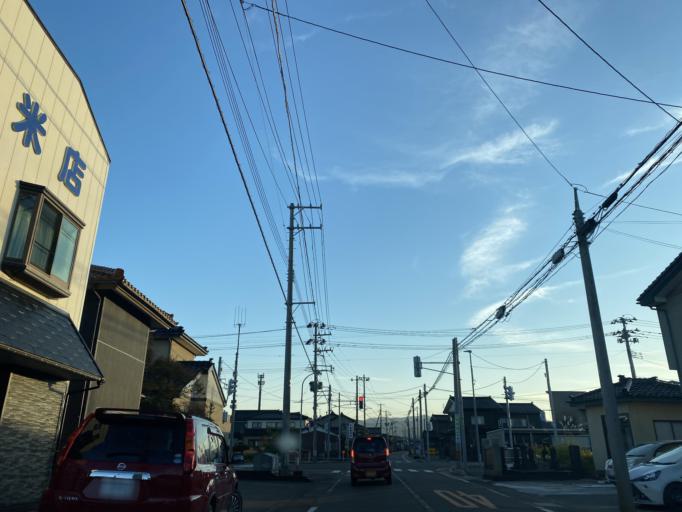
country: JP
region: Niigata
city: Kashiwazaki
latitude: 37.3805
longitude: 138.5675
